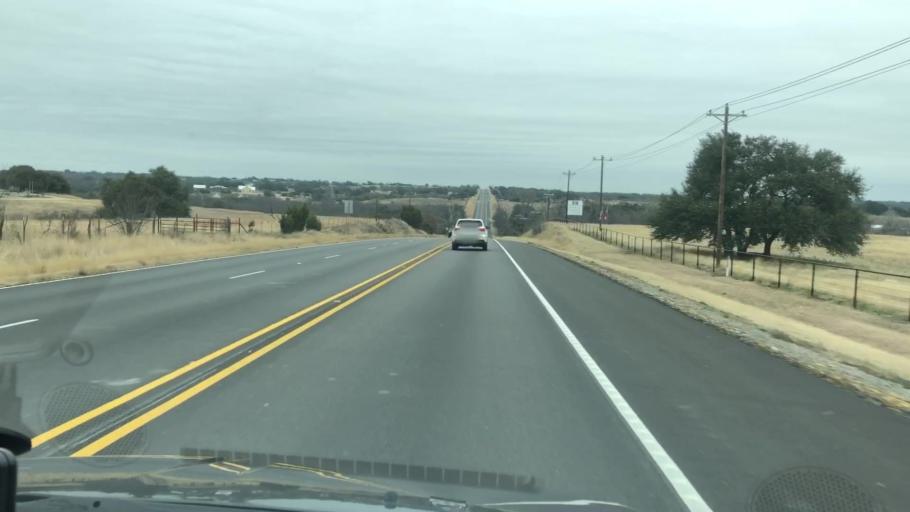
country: US
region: Texas
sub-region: Erath County
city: Stephenville
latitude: 32.3109
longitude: -98.1845
